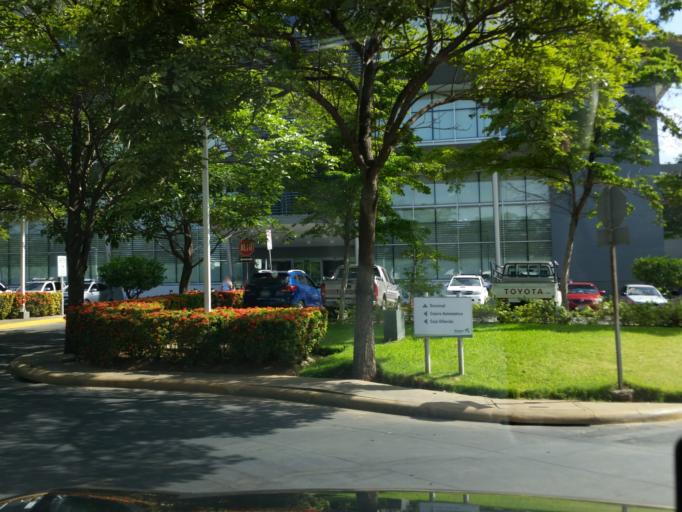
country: NI
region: Managua
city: Managua
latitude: 12.1346
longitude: -86.2796
